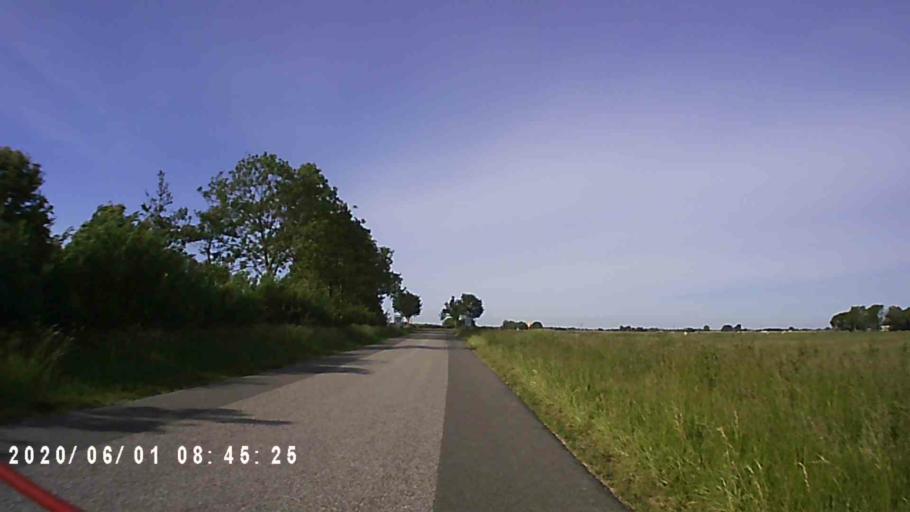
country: NL
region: Friesland
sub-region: Gemeente Ferwerderadiel
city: Burdaard
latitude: 53.2774
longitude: 5.8349
